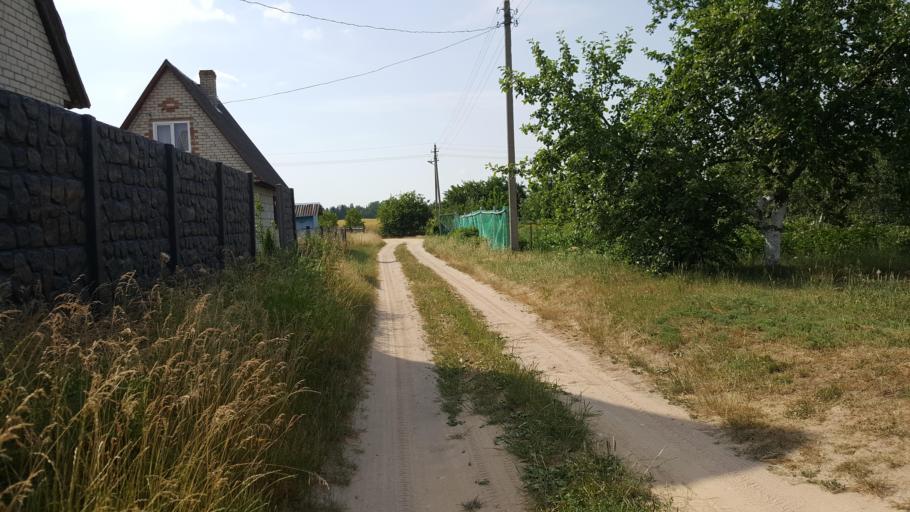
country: BY
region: Brest
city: Kamyanyets
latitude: 52.3696
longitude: 23.8030
